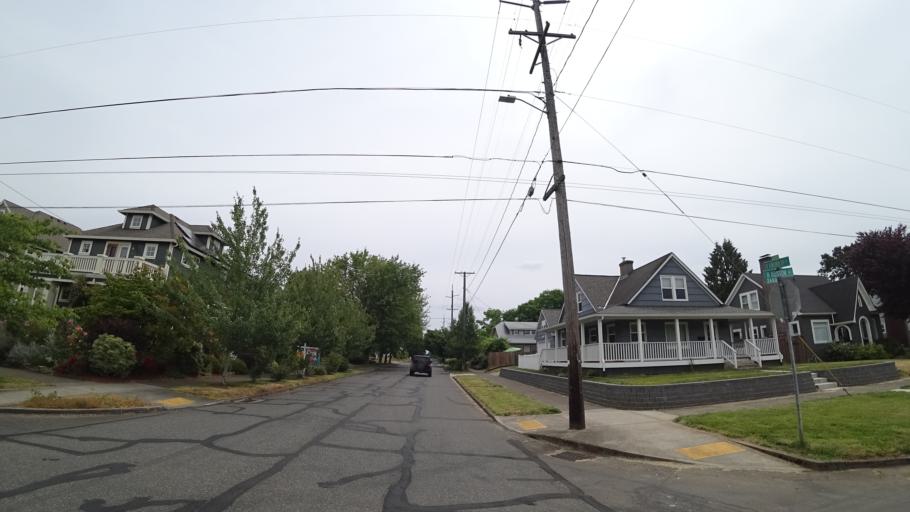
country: US
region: Oregon
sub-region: Multnomah County
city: Portland
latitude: 45.5664
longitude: -122.6914
